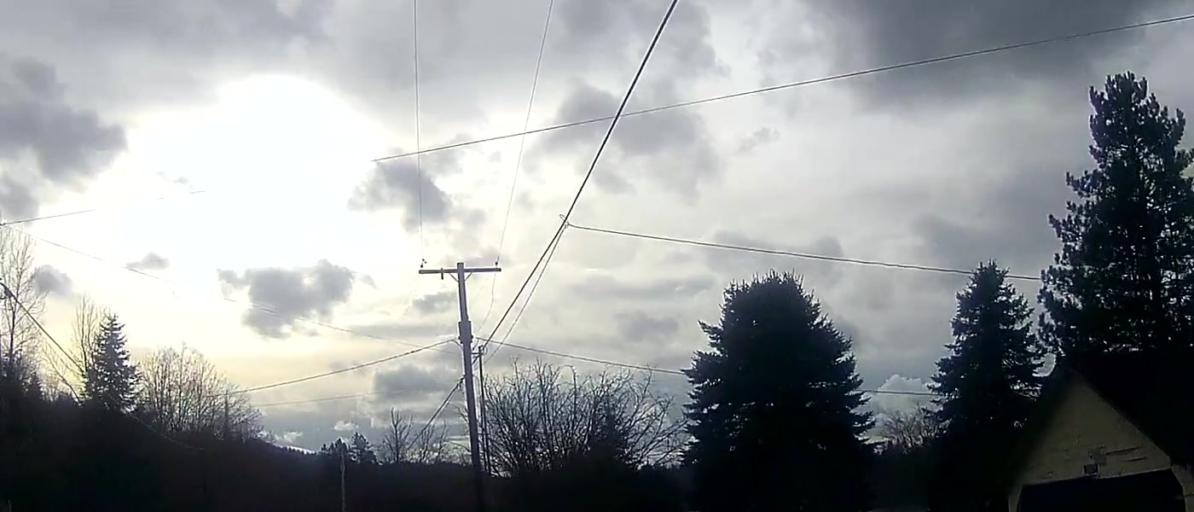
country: US
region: Washington
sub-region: Skagit County
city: Sedro-Woolley
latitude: 48.5754
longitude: -122.2981
